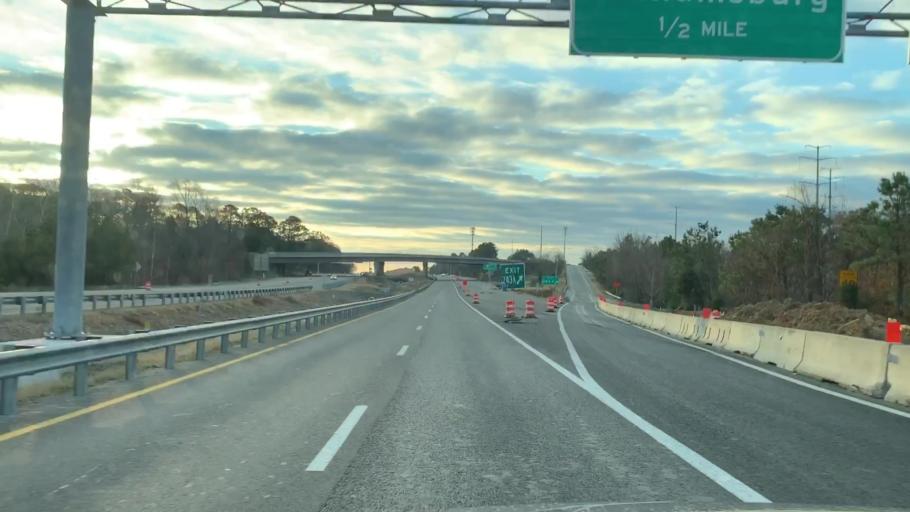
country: US
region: Virginia
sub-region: City of Williamsburg
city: Williamsburg
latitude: 37.2447
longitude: -76.6367
